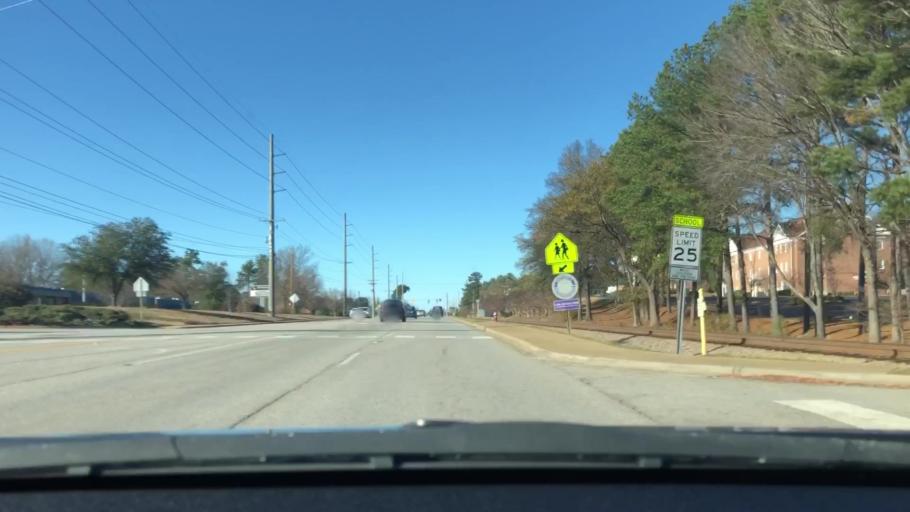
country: US
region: South Carolina
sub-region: Lexington County
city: Irmo
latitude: 34.0727
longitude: -81.1756
